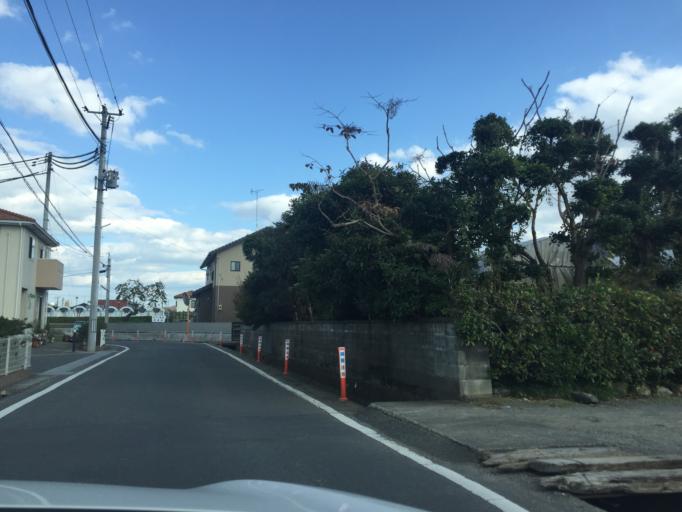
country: JP
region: Fukushima
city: Iwaki
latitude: 37.0595
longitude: 140.8655
